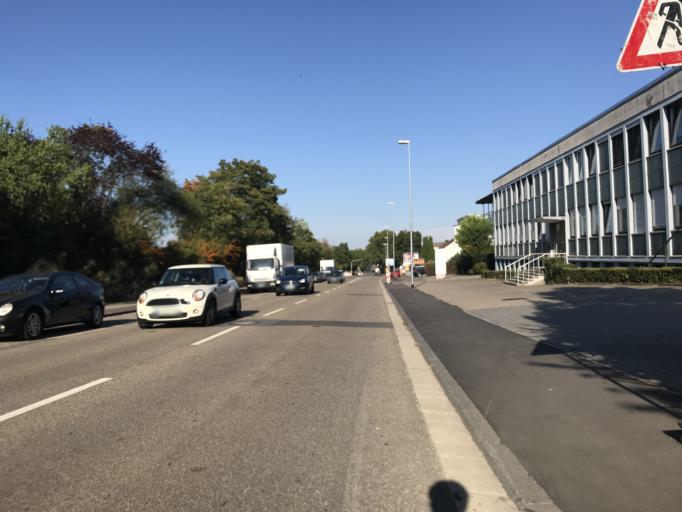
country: DE
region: Rheinland-Pfalz
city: Mainz
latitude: 49.9768
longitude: 8.2854
